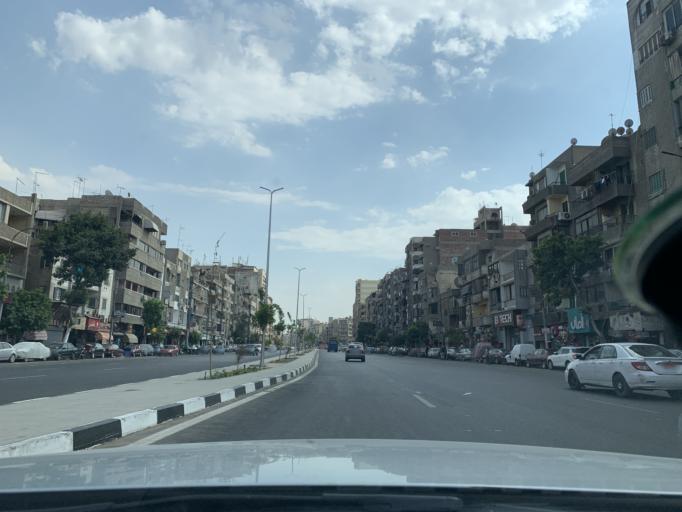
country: EG
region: Muhafazat al Qalyubiyah
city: Al Khankah
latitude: 30.1089
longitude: 31.3449
